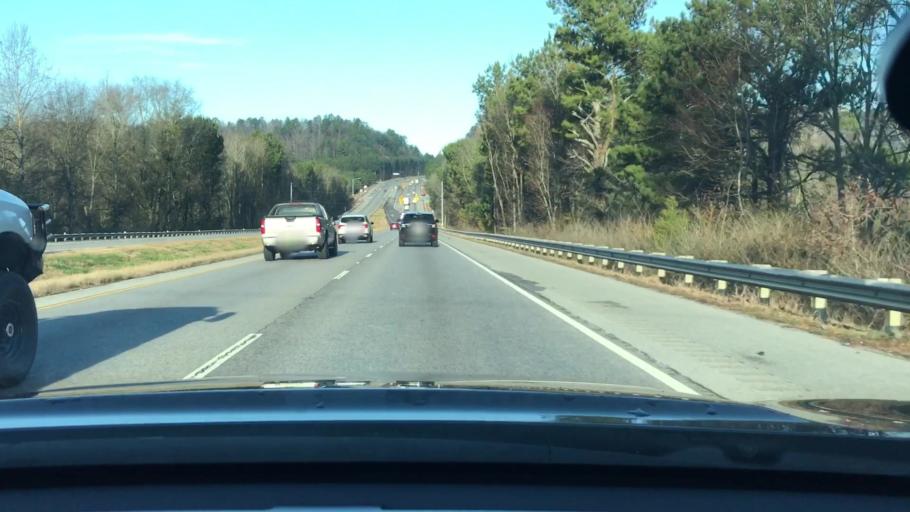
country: US
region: Alabama
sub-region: Shelby County
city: Chelsea
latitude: 33.3531
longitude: -86.6468
